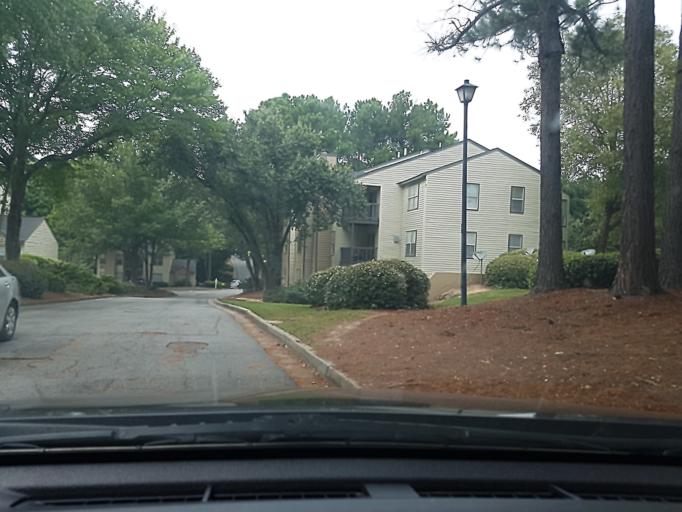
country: US
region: Georgia
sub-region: Gwinnett County
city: Berkeley Lake
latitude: 33.9530
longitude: -84.1479
